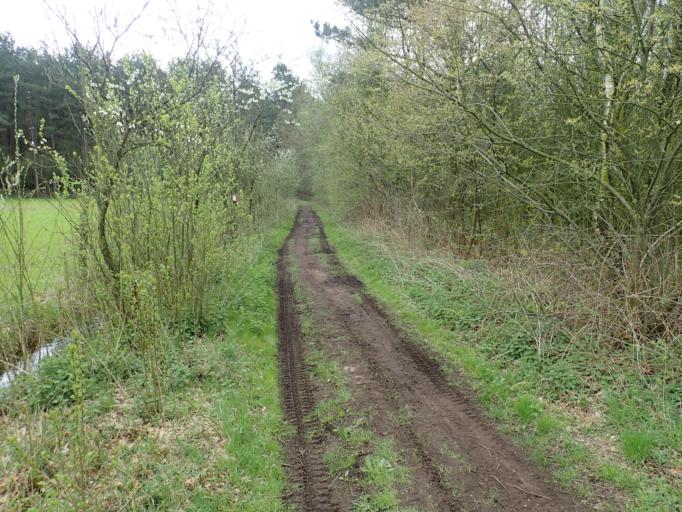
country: BE
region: Flanders
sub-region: Provincie Antwerpen
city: Lille
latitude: 51.2275
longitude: 4.8069
